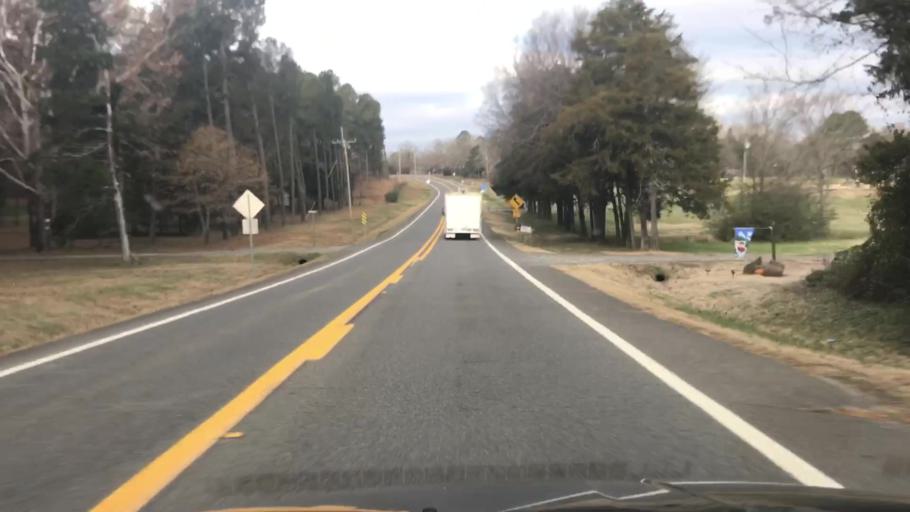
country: US
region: Arkansas
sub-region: Montgomery County
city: Mount Ida
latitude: 34.6221
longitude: -93.7246
